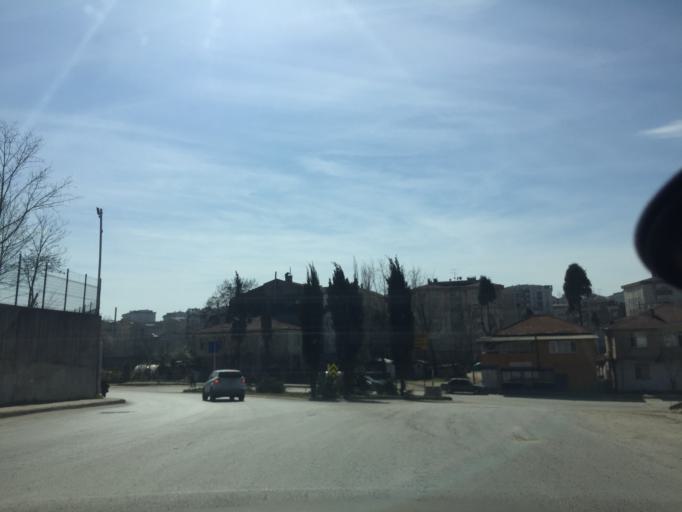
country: TR
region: Istanbul
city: Icmeler
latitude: 40.8367
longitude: 29.3148
